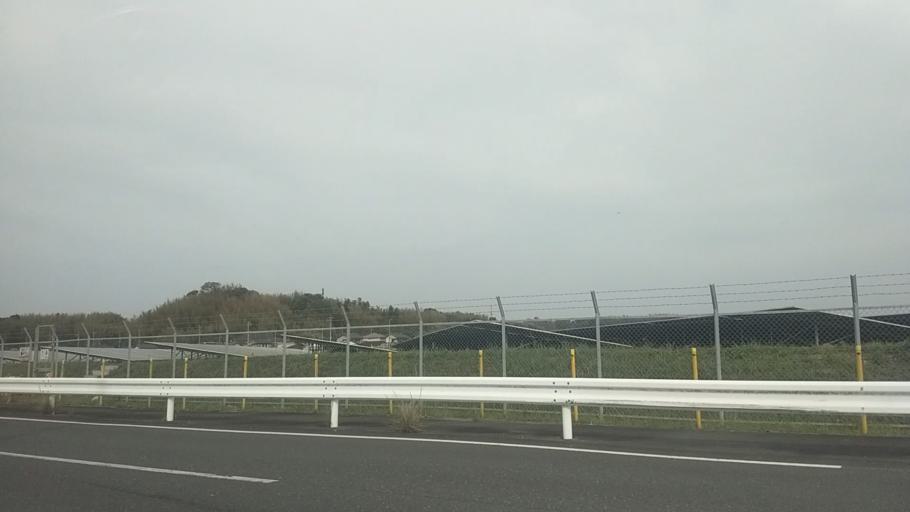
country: JP
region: Shizuoka
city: Kosai-shi
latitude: 34.7391
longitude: 137.6093
